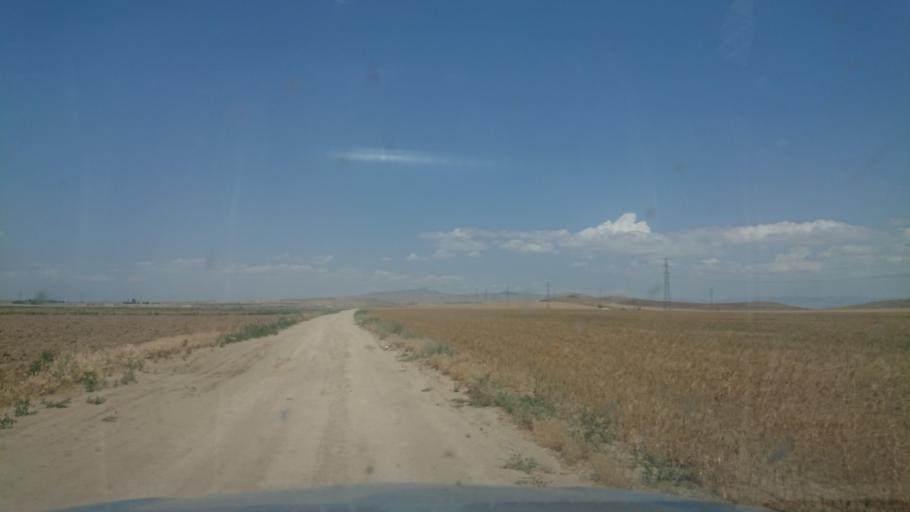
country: TR
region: Aksaray
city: Sariyahsi
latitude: 39.0136
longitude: 33.8773
